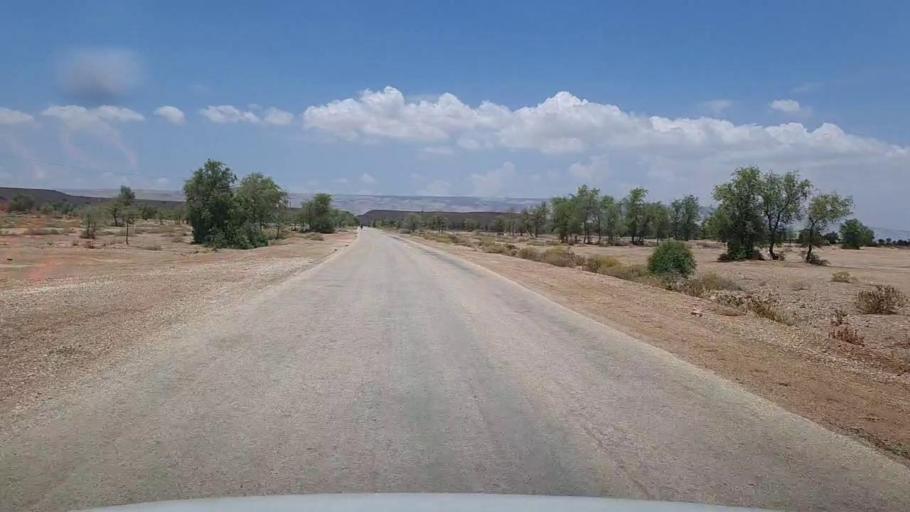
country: PK
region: Sindh
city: Bhan
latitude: 26.3176
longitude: 67.5983
